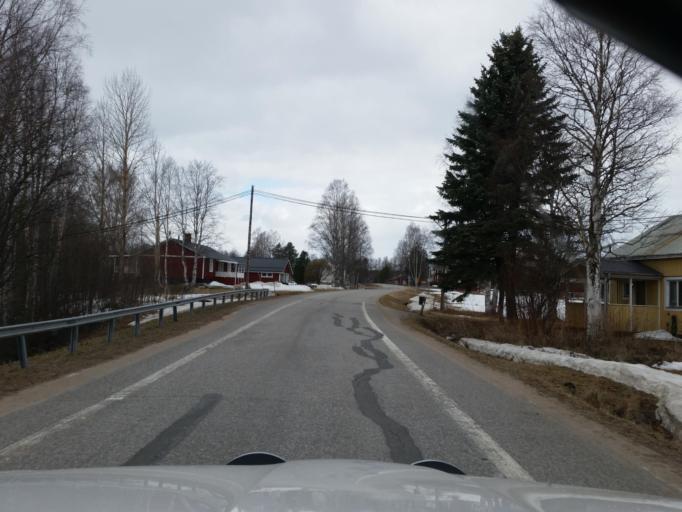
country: SE
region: Norrbotten
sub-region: Pitea Kommun
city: Roknas
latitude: 65.3464
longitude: 21.1856
